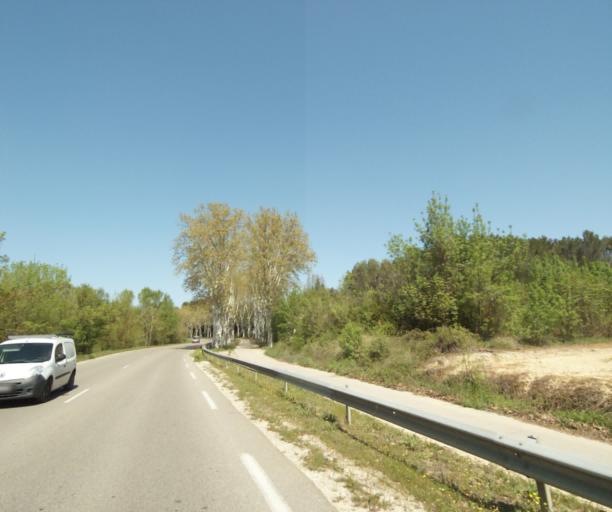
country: FR
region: Languedoc-Roussillon
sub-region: Departement de l'Herault
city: Prades-le-Lez
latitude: 43.6807
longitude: 3.8656
